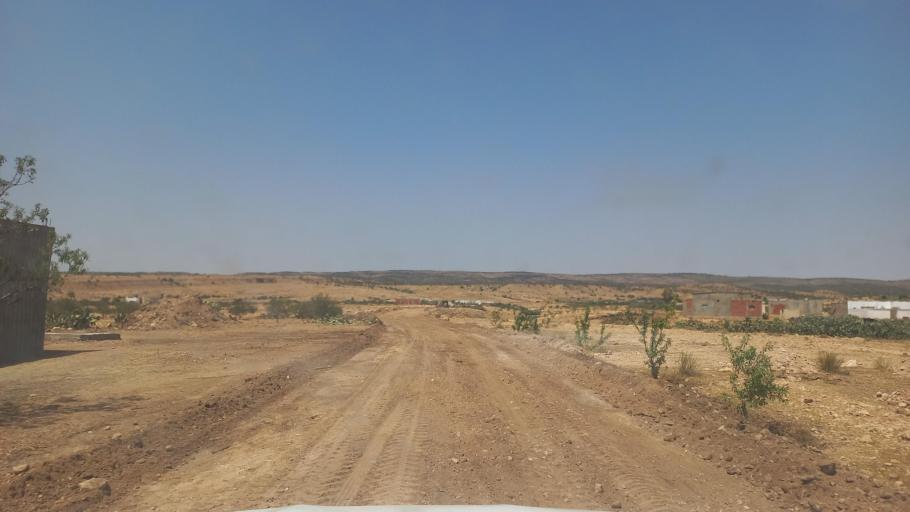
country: TN
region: Al Qasrayn
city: Kasserine
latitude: 35.2960
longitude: 8.9426
